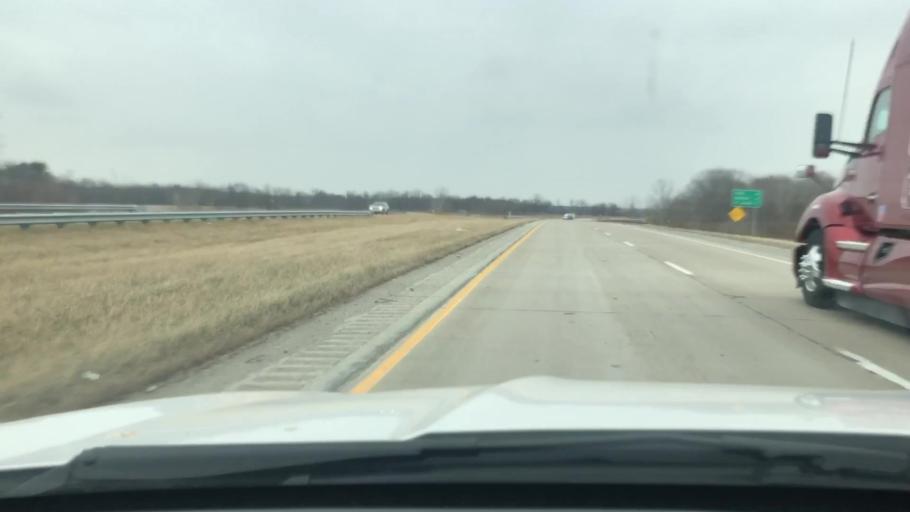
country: US
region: Indiana
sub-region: Cass County
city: Logansport
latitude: 40.7323
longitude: -86.3049
